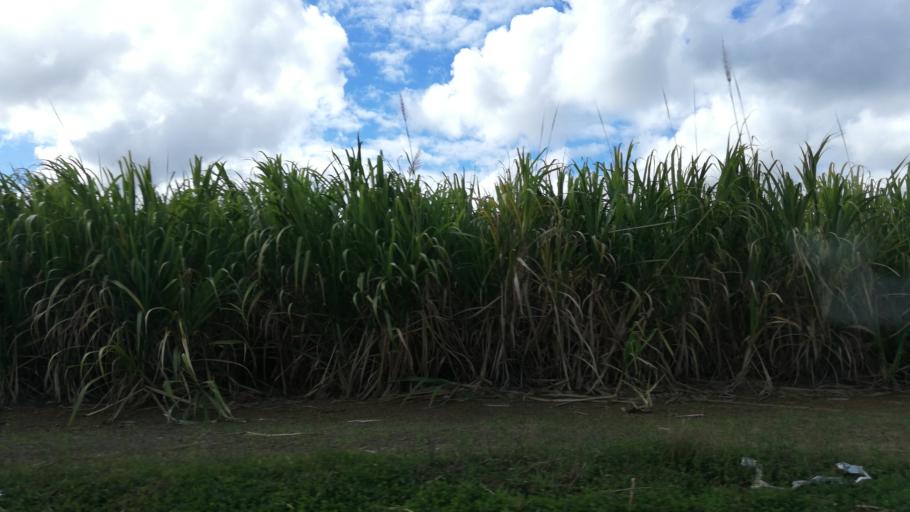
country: MU
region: Flacq
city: Camp de Masque
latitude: -20.2152
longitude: 57.6754
